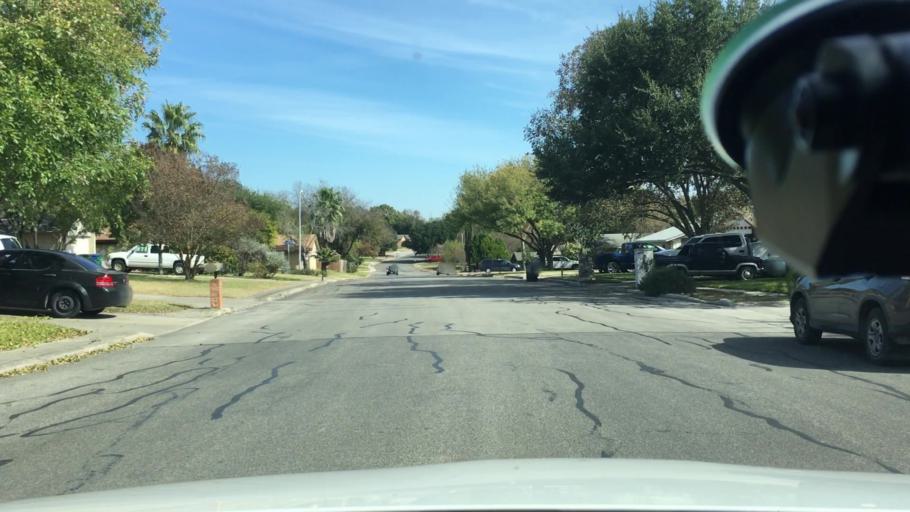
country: US
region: Texas
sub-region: Bexar County
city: Windcrest
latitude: 29.5722
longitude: -98.4168
